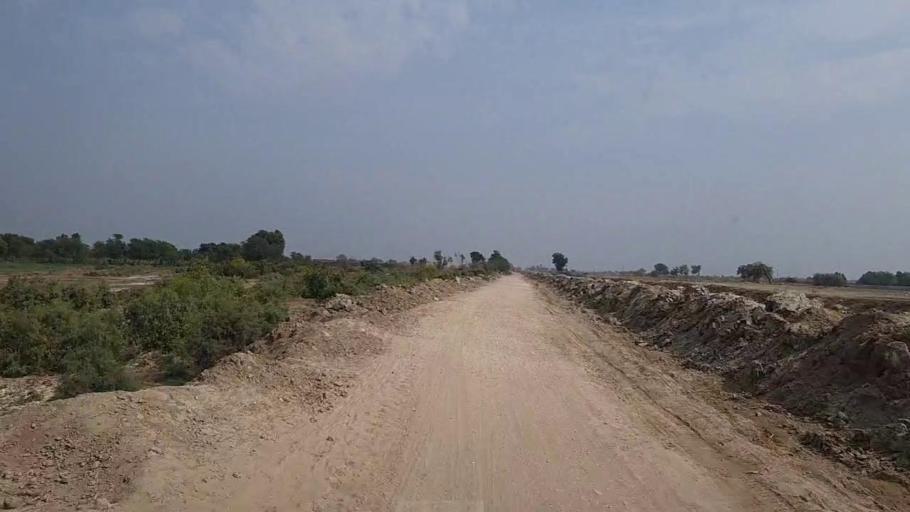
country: PK
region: Sindh
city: Mirwah Gorchani
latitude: 25.3999
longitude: 69.0809
